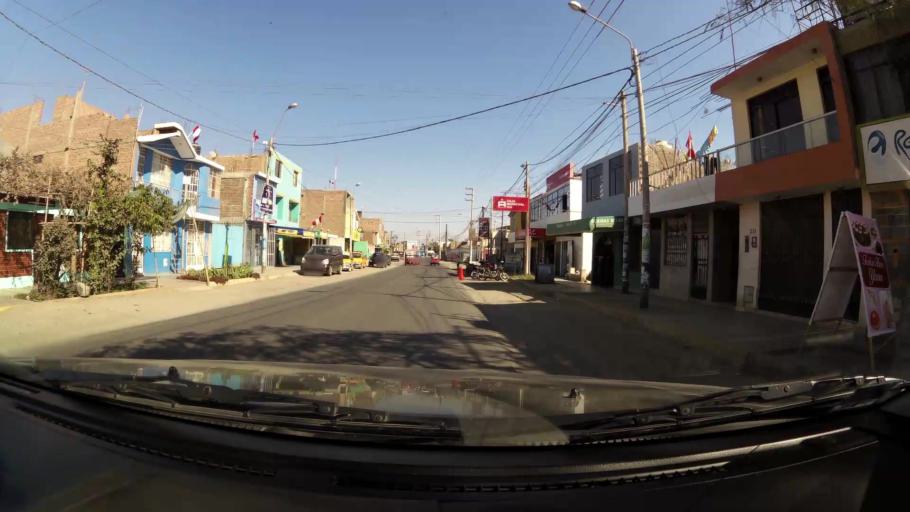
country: PE
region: Ica
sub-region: Provincia de Ica
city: La Tinguina
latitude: -14.0382
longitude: -75.7110
